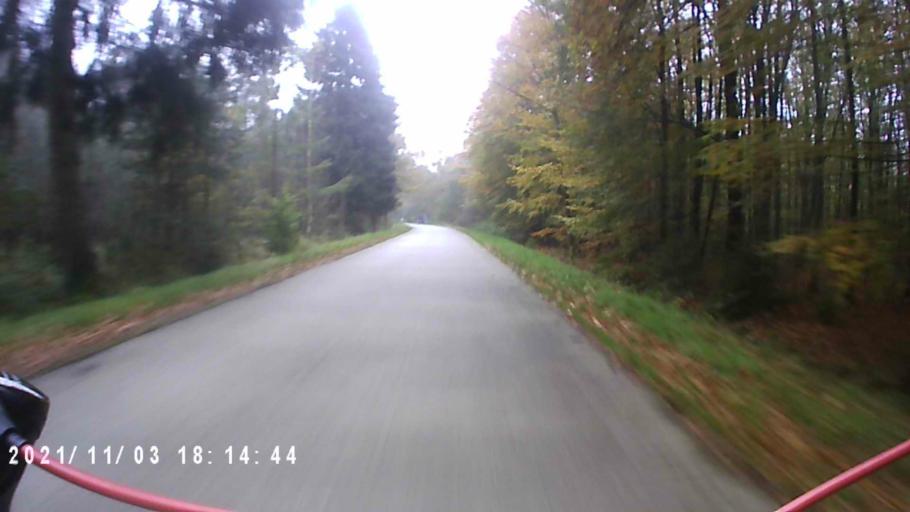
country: NL
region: Drenthe
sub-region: Gemeente Westerveld
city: Dwingeloo
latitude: 52.8156
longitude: 6.3953
